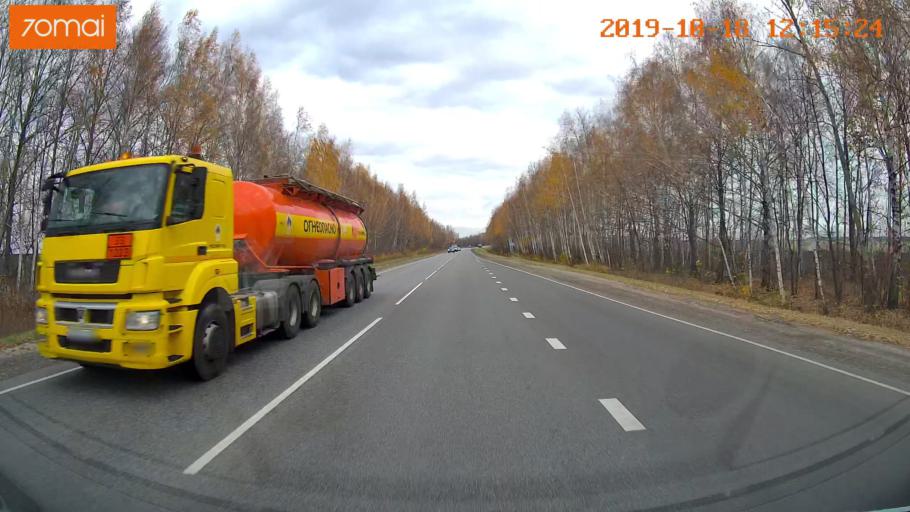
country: RU
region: Rjazan
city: Zakharovo
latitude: 54.4429
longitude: 39.3995
